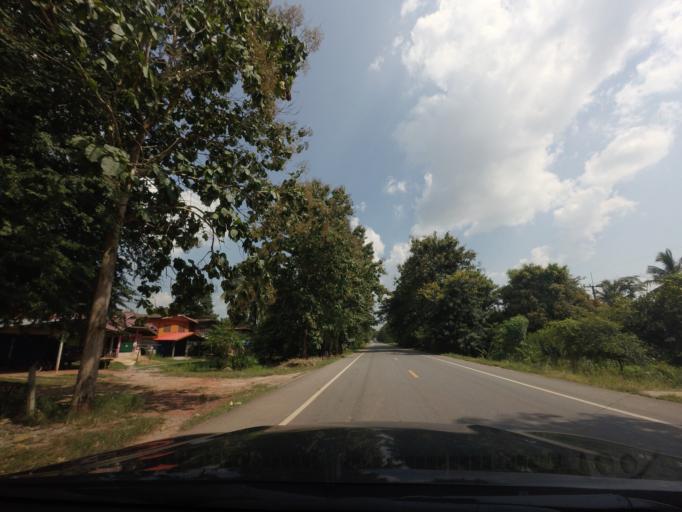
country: TH
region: Phitsanulok
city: Chat Trakan
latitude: 17.2893
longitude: 100.5171
